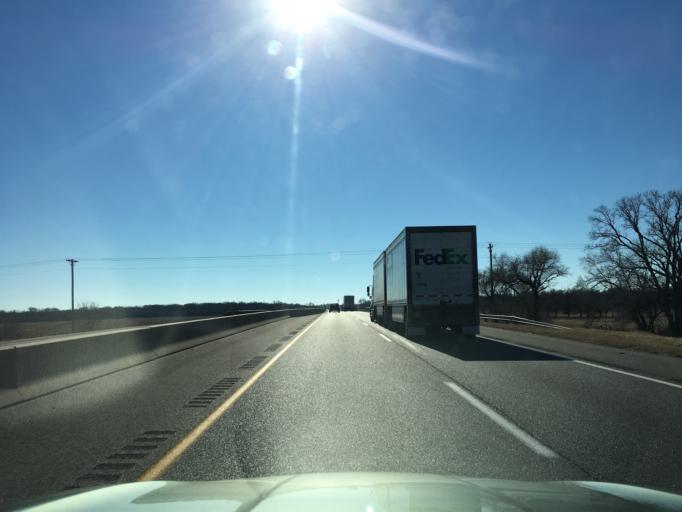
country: US
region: Kansas
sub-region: Sumner County
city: Belle Plaine
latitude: 37.3934
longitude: -97.3259
